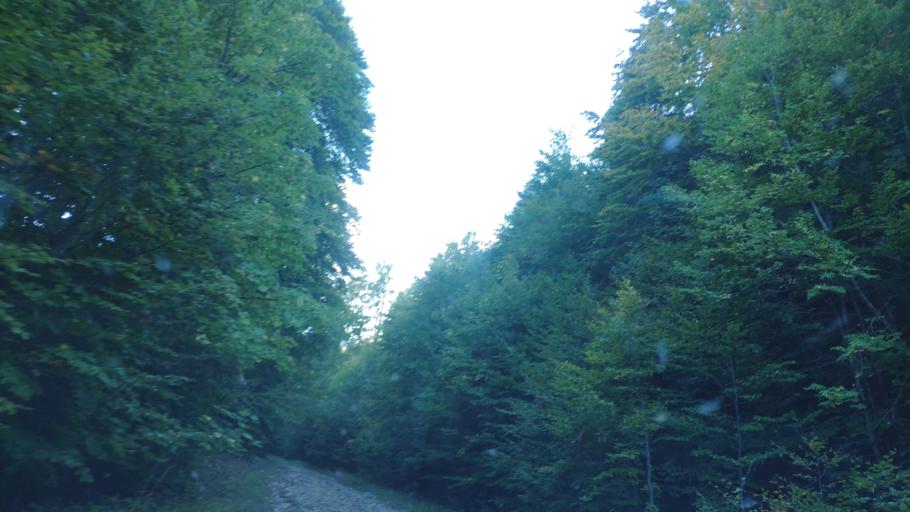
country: AL
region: Korce
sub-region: Rrethi i Devollit
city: Miras
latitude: 40.3586
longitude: 20.8965
